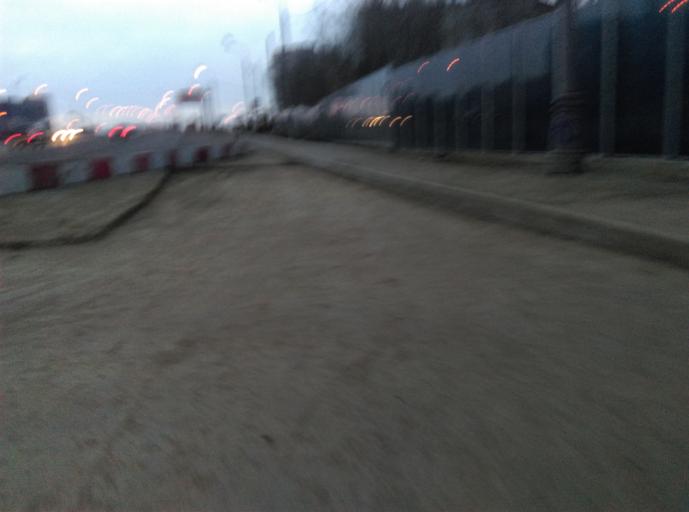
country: RU
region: Moskovskaya
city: Vostryakovo
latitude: 55.6725
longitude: 37.4482
